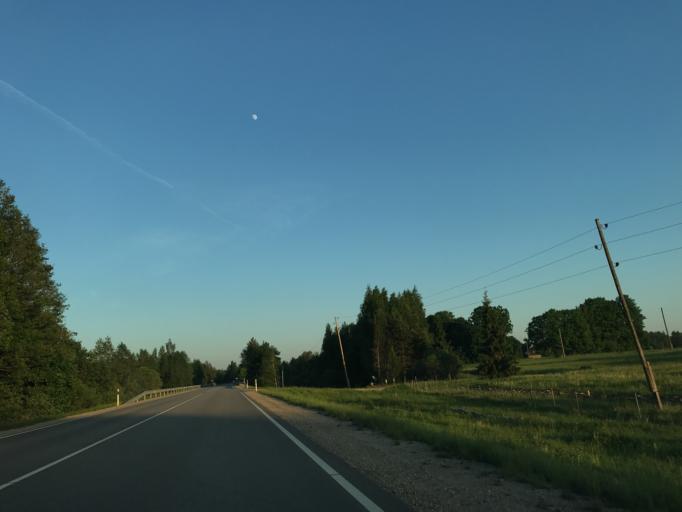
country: LV
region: Lielvarde
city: Lielvarde
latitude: 56.4842
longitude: 24.7800
